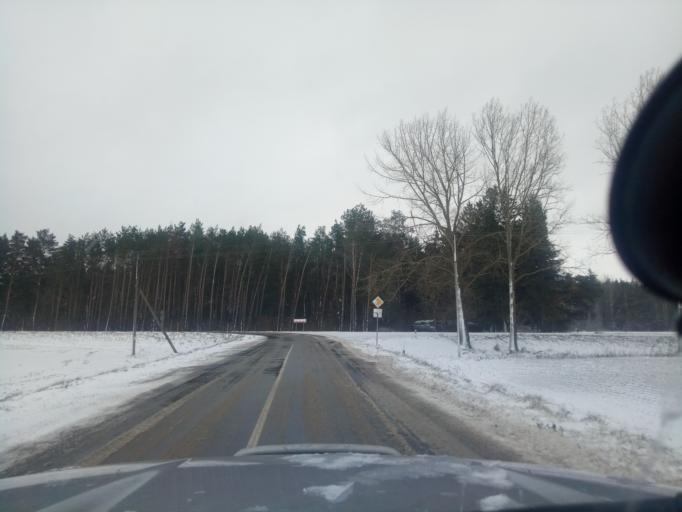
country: BY
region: Minsk
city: Tsimkavichy
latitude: 53.0427
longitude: 26.8436
